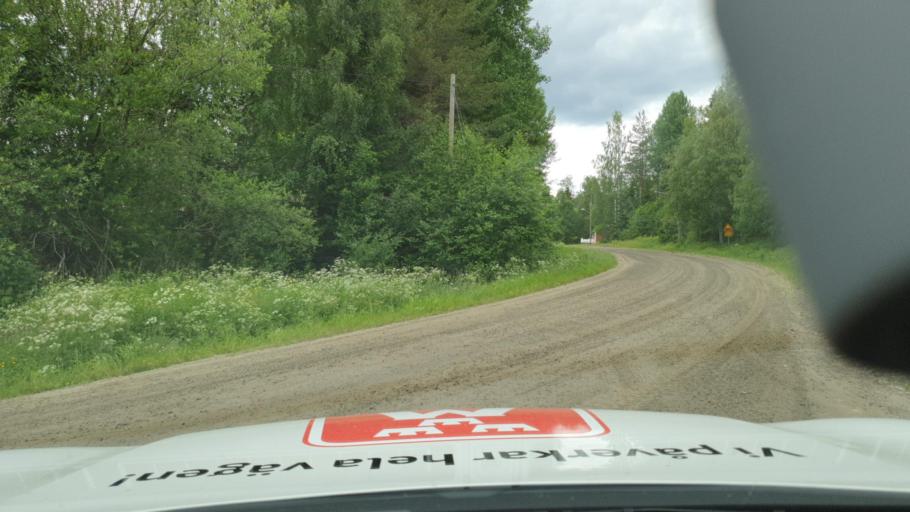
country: SE
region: Vaesterbotten
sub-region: Bjurholms Kommun
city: Bjurholm
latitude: 63.8141
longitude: 19.0337
